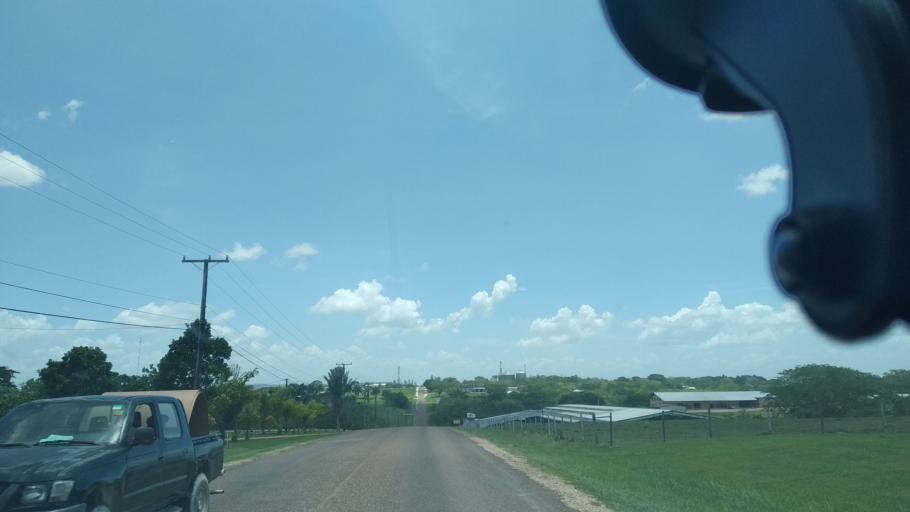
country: BZ
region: Cayo
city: San Ignacio
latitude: 17.2566
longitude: -88.9901
